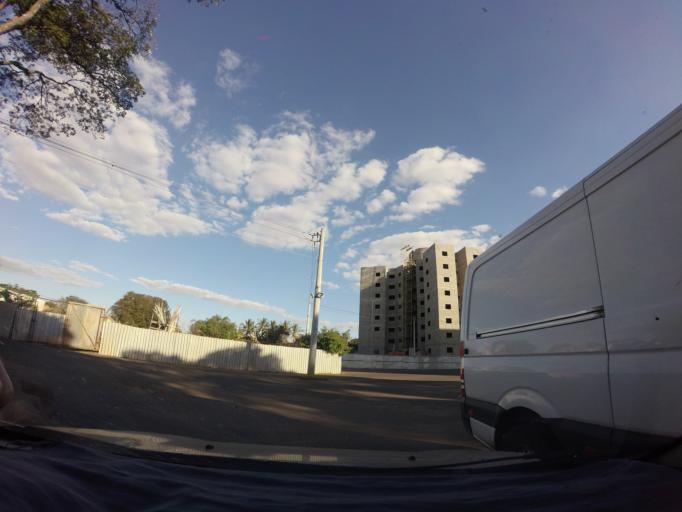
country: BR
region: Sao Paulo
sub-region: Piracicaba
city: Piracicaba
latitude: -22.7389
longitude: -47.5959
